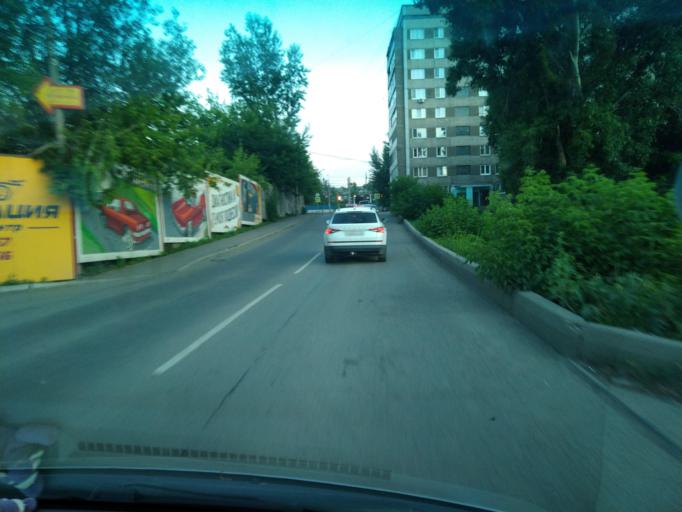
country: RU
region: Krasnoyarskiy
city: Krasnoyarsk
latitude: 55.9843
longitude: 92.8716
